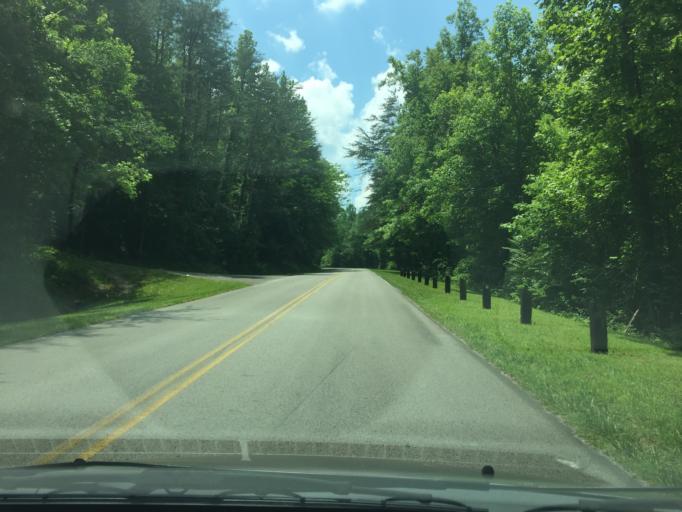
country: US
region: Tennessee
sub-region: Hamilton County
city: Lookout Mountain
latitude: 35.0543
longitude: -85.4230
